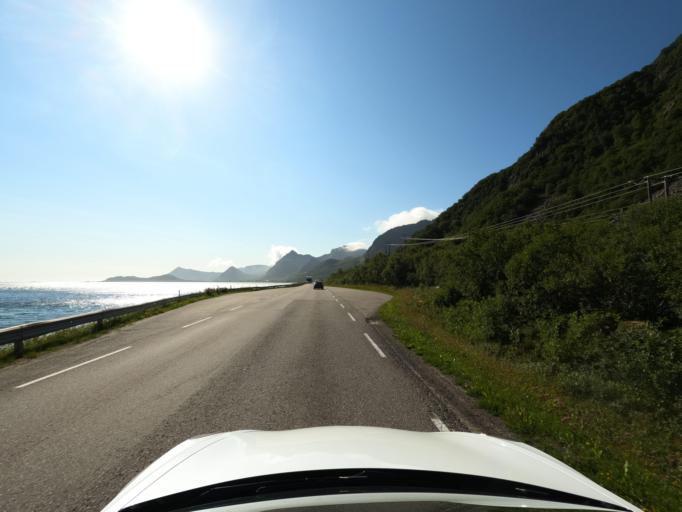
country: NO
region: Nordland
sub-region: Vagan
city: Kabelvag
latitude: 68.2579
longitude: 14.2106
